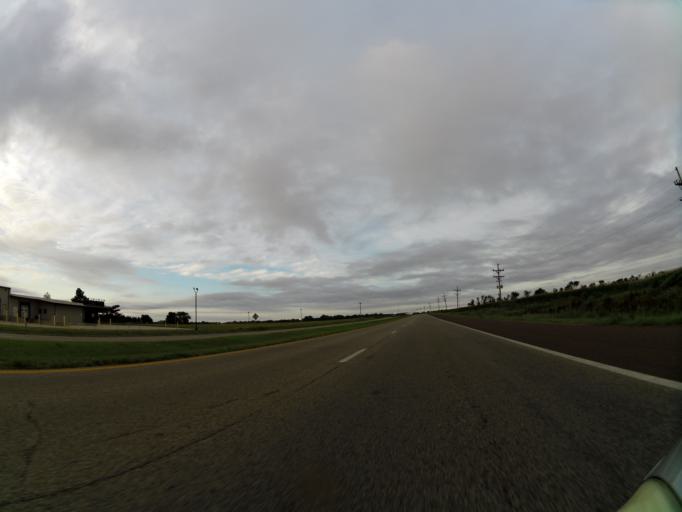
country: US
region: Kansas
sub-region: Reno County
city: South Hutchinson
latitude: 38.0020
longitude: -97.9406
